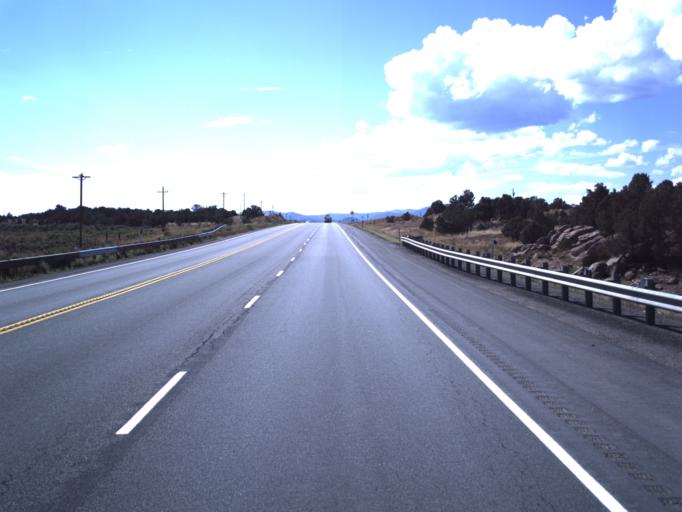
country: US
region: Utah
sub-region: Duchesne County
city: Duchesne
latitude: 40.2052
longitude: -110.8028
